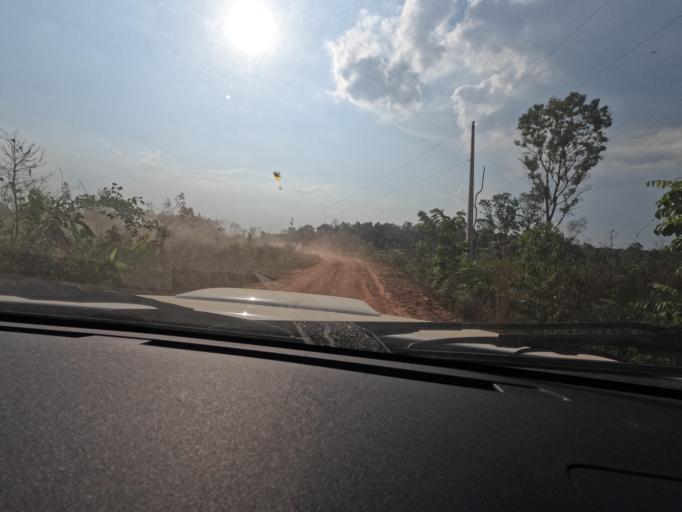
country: BR
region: Rondonia
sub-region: Porto Velho
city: Porto Velho
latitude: -8.5736
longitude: -64.0117
